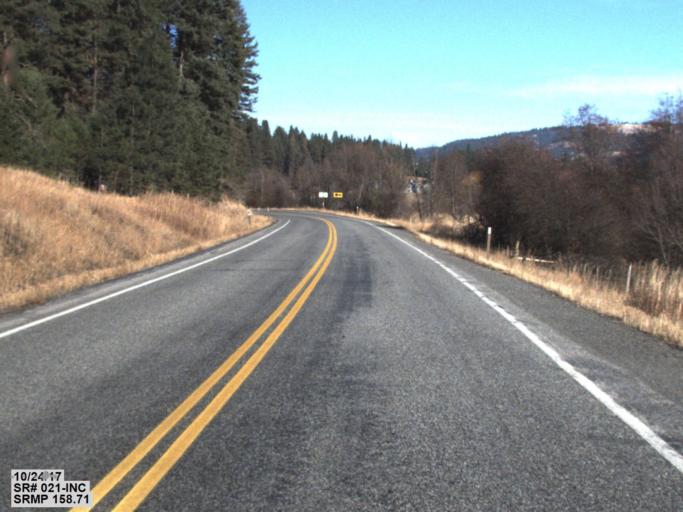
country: US
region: Washington
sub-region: Ferry County
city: Republic
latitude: 48.6216
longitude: -118.7303
